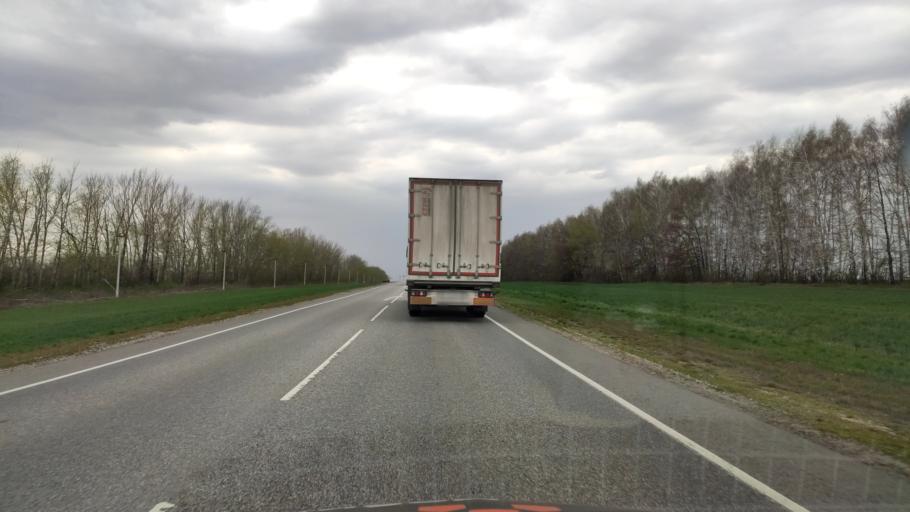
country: RU
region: Kursk
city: Gorshechnoye
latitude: 51.5493
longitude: 38.1485
